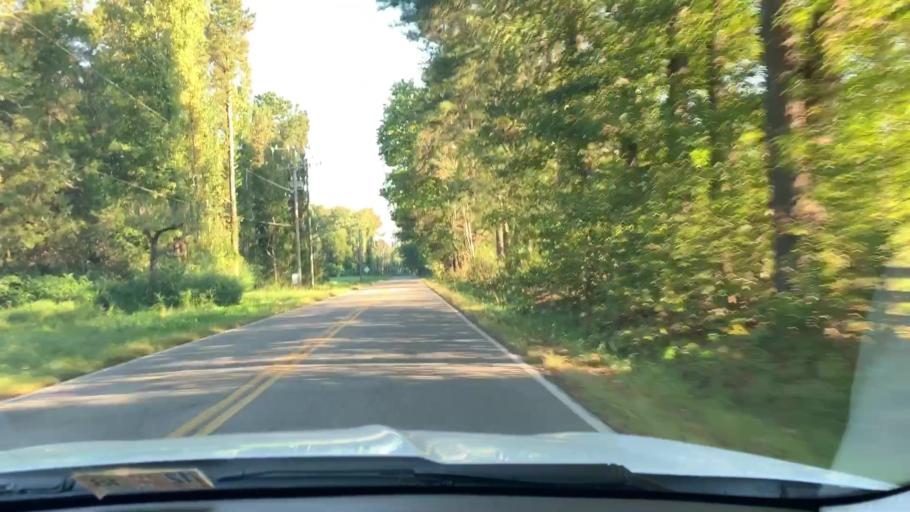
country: US
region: Virginia
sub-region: Middlesex County
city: Deltaville
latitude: 37.5551
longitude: -76.4515
